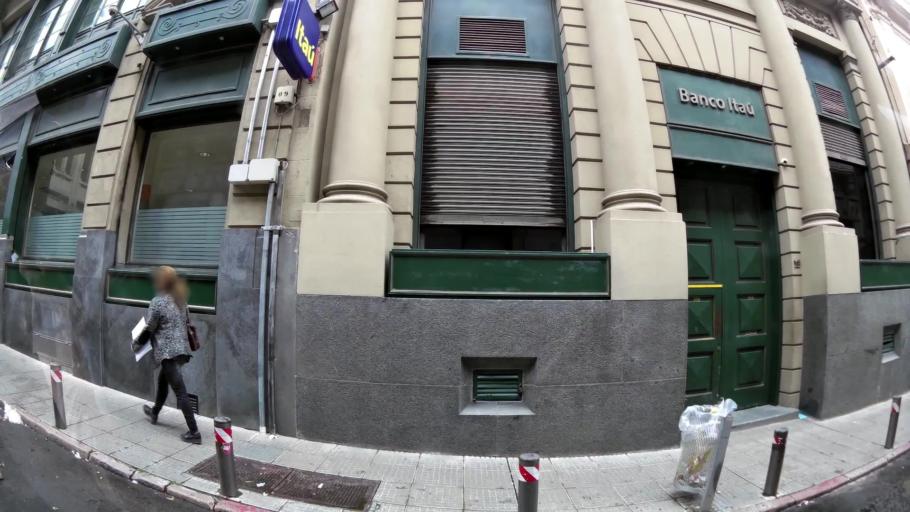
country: UY
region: Montevideo
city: Montevideo
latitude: -34.9064
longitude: -56.2079
